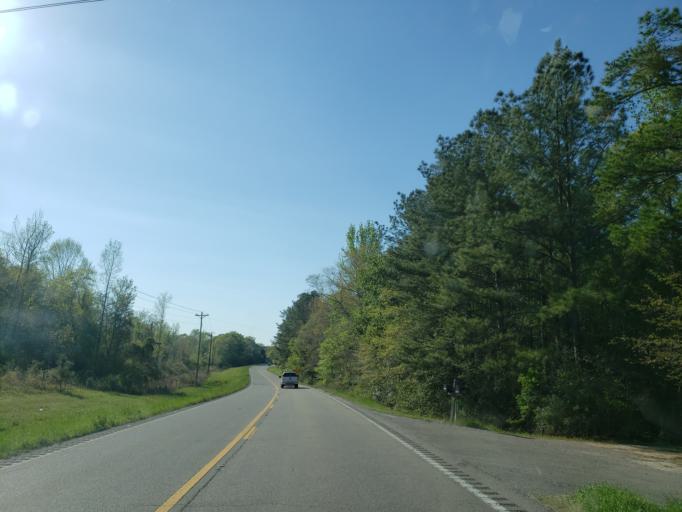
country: US
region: Mississippi
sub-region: Perry County
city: Richton
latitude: 31.4698
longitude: -88.9959
